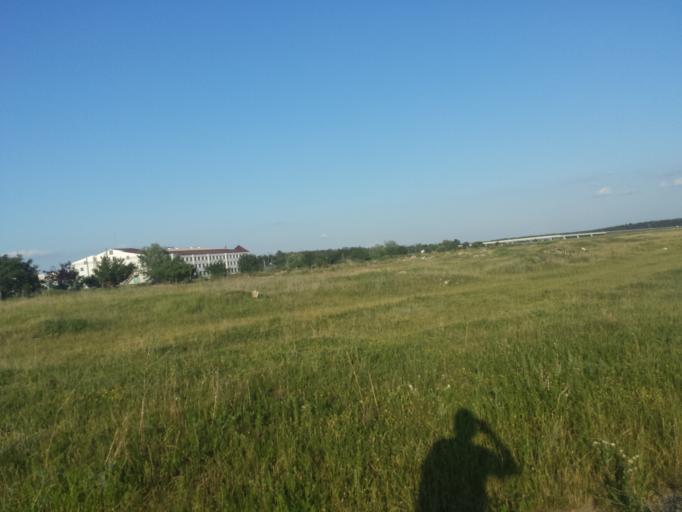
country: RO
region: Ilfov
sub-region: Comuna Tunari
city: Tunari
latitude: 44.5291
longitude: 26.1522
